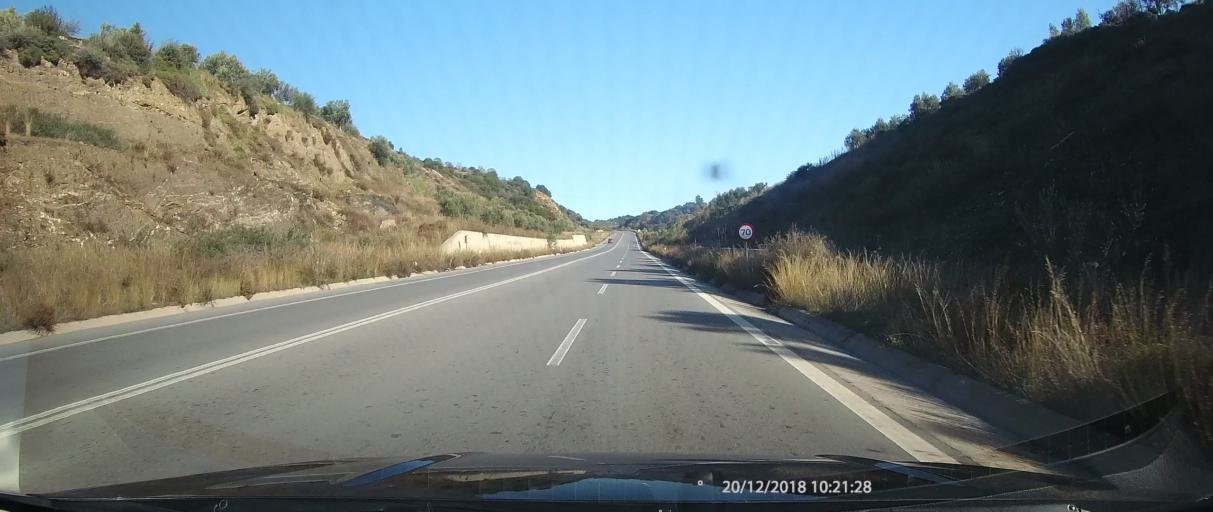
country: GR
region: Peloponnese
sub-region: Nomos Lakonias
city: Magoula
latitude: 37.1600
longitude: 22.4253
